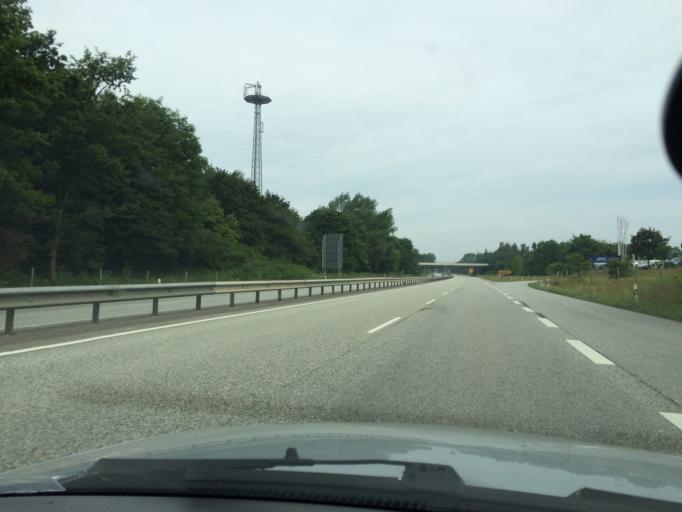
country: DE
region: Schleswig-Holstein
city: Flensburg
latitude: 54.7659
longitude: 9.4252
